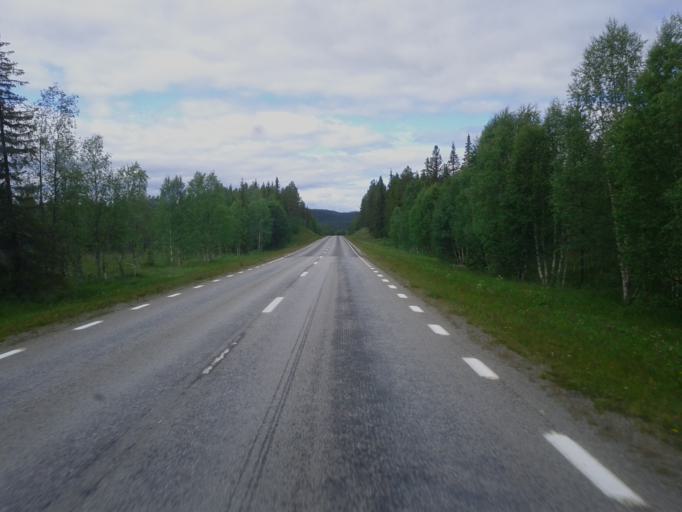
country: SE
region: Vaesterbotten
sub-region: Storumans Kommun
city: Fristad
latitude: 65.3574
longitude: 16.5533
